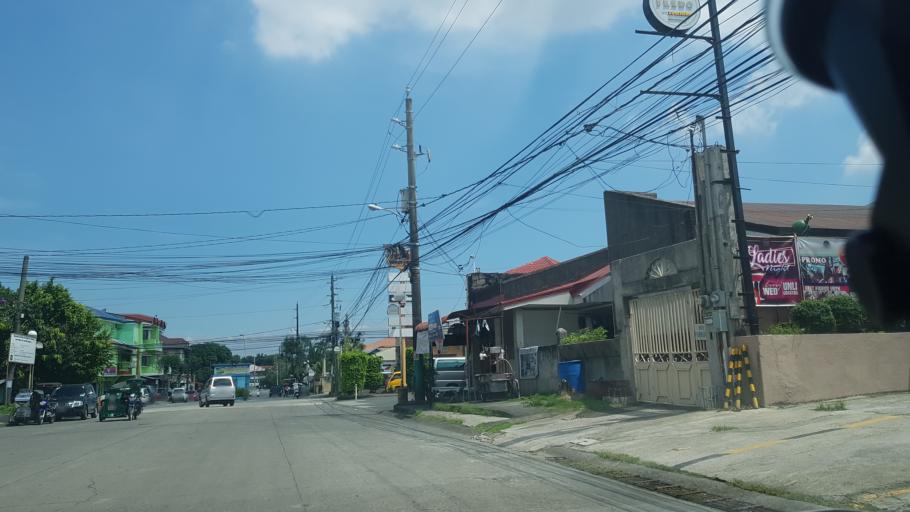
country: PH
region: Calabarzon
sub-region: Province of Rizal
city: Las Pinas
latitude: 14.4300
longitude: 120.9896
